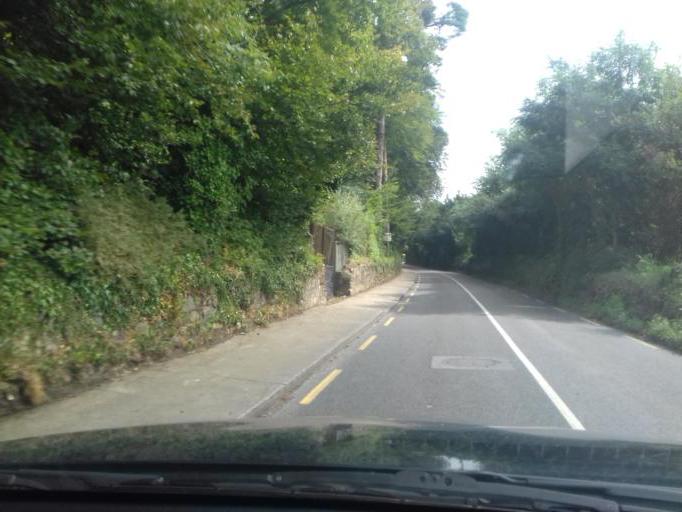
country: IE
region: Leinster
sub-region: Loch Garman
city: Enniscorthy
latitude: 52.5071
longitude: -6.5537
